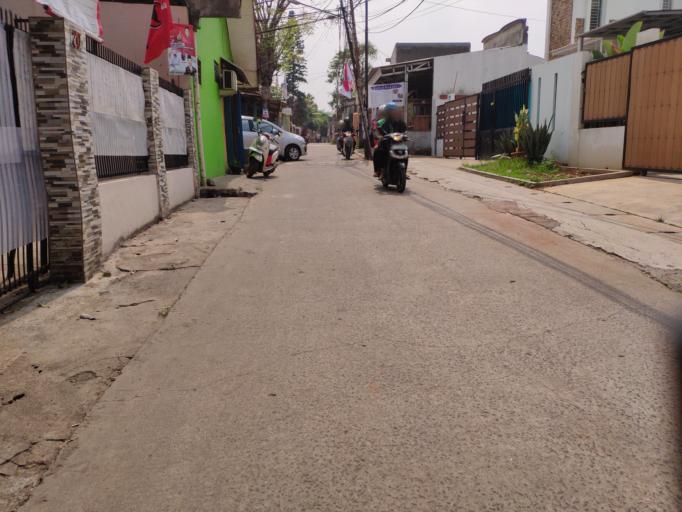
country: ID
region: West Java
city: Pamulang
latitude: -6.3214
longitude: 106.8011
